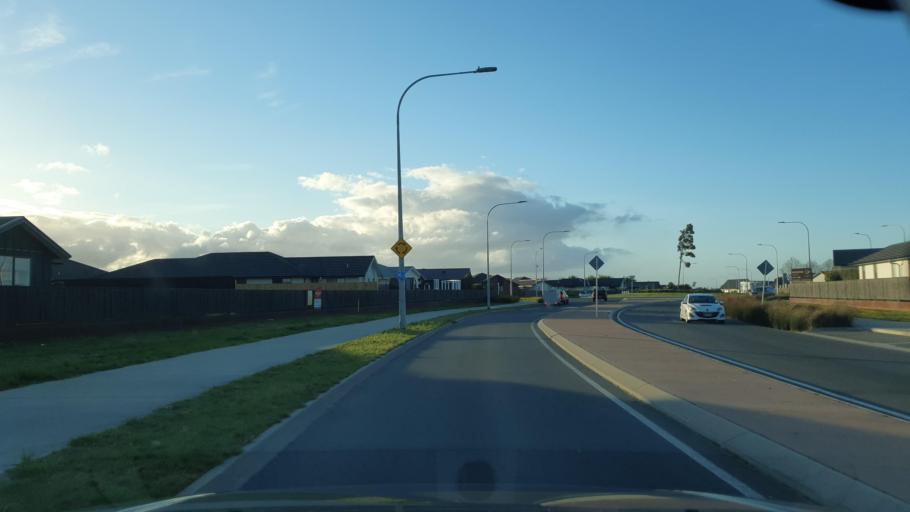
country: NZ
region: Bay of Plenty
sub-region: Western Bay of Plenty District
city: Maketu
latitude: -37.7201
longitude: 176.3155
